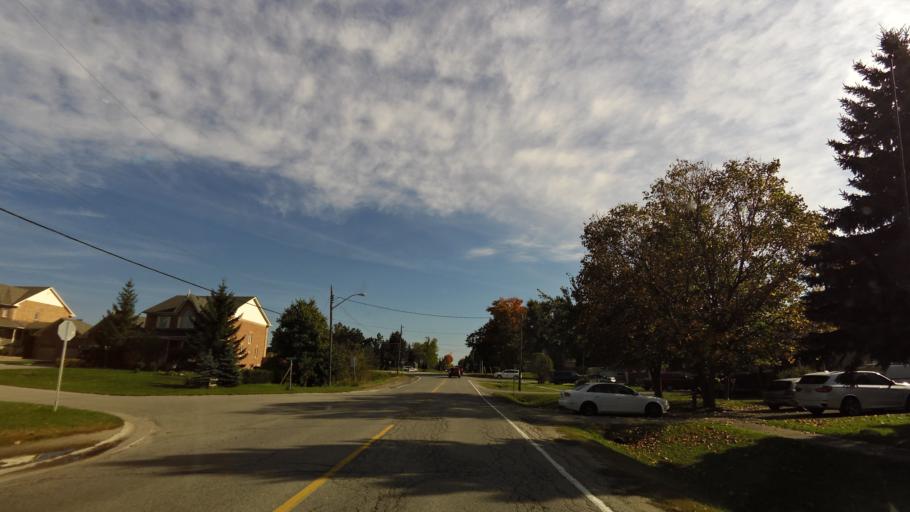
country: CA
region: Ontario
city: Orangeville
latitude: 43.7641
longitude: -80.0555
